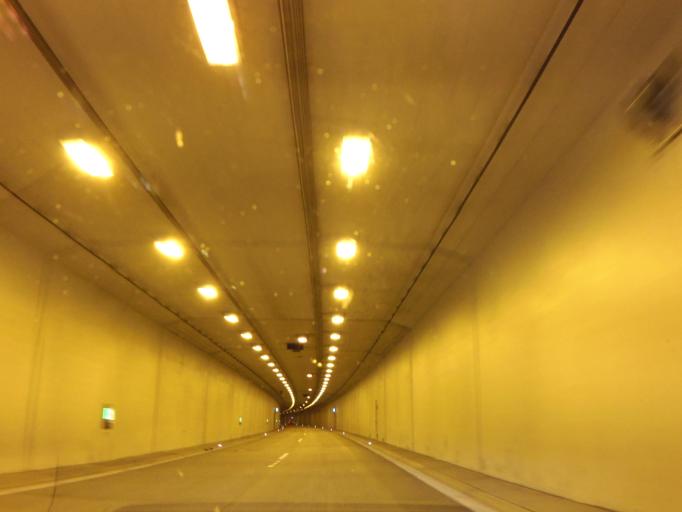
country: DE
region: Bavaria
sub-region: Swabia
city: Hopferau
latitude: 47.5992
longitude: 10.6568
